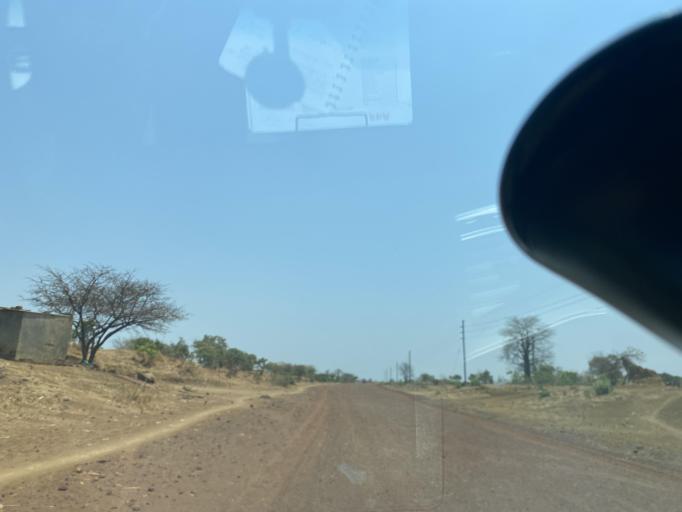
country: ZM
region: Southern
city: Nakambala
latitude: -15.4769
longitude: 27.8977
